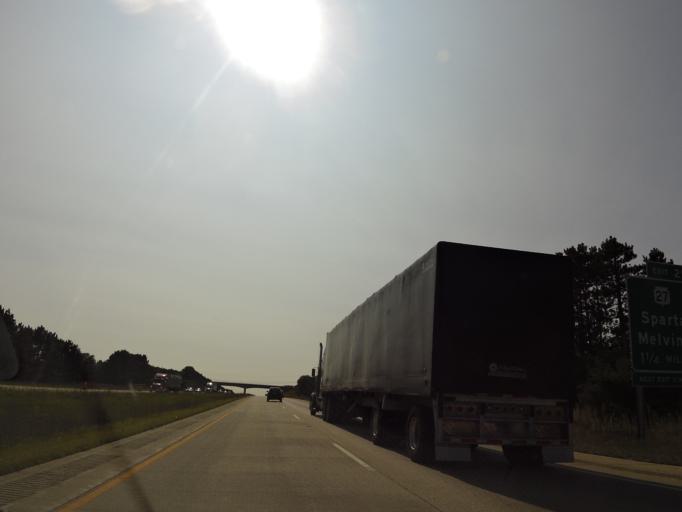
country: US
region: Wisconsin
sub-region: Monroe County
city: Sparta
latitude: 43.9281
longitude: -90.7918
